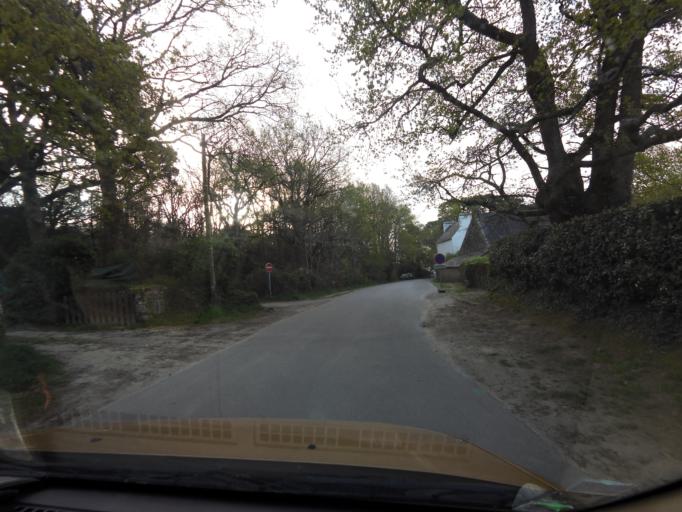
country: FR
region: Brittany
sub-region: Departement du Morbihan
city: Arradon
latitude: 47.6236
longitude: -2.8141
